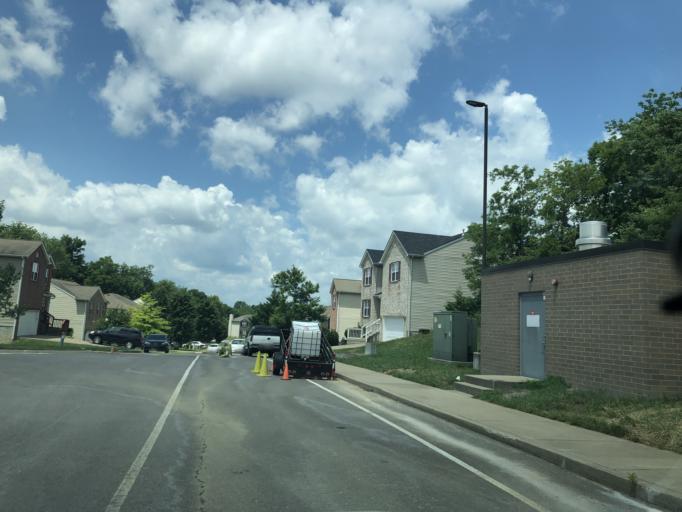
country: US
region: Tennessee
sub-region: Rutherford County
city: La Vergne
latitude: 36.0411
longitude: -86.6180
